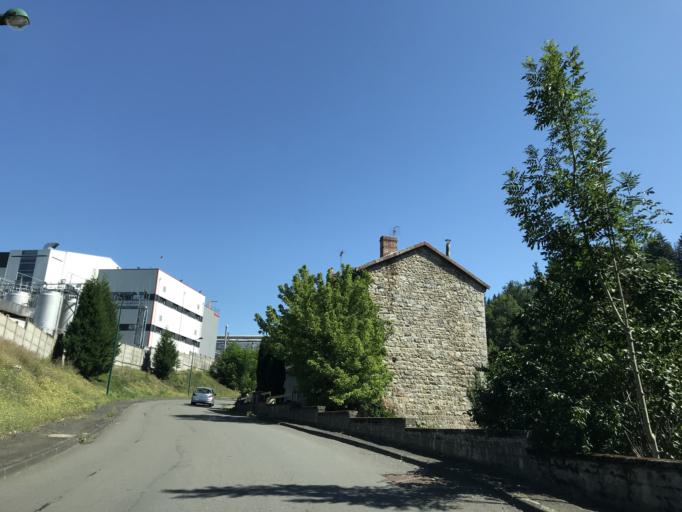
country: FR
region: Auvergne
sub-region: Departement du Puy-de-Dome
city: Job
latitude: 45.6459
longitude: 3.7054
